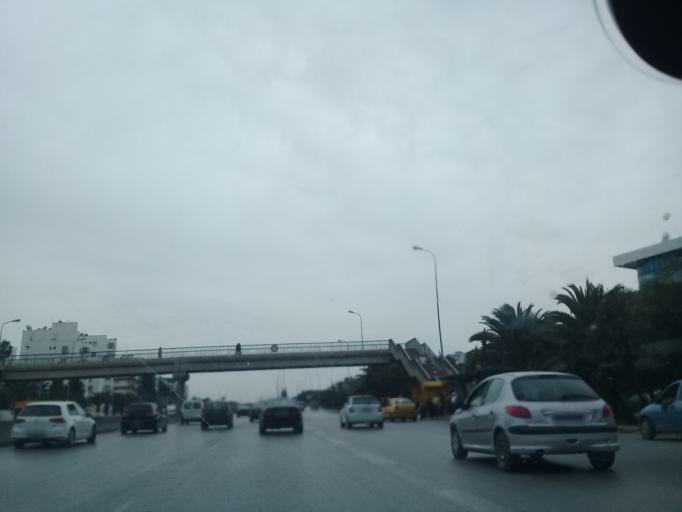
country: TN
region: Tunis
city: Tunis
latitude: 36.8362
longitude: 10.1610
